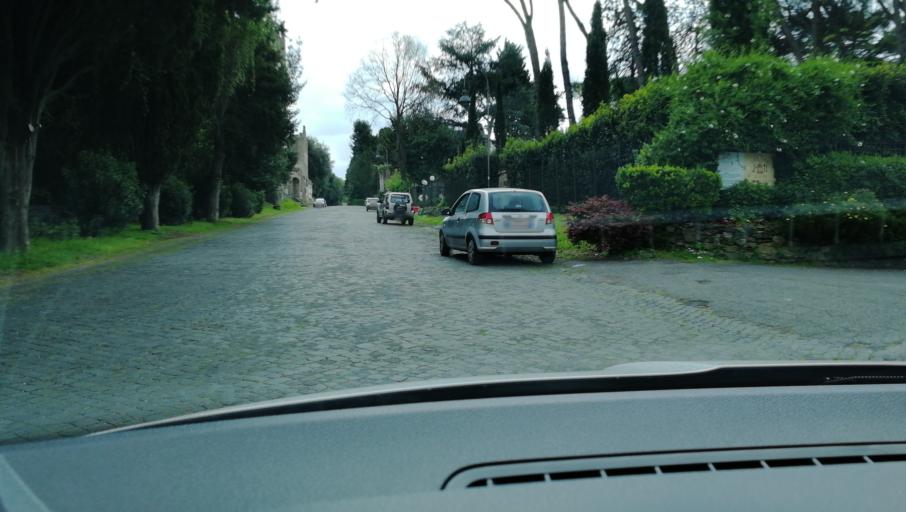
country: IT
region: Latium
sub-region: Citta metropolitana di Roma Capitale
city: Rome
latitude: 41.8528
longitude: 12.5197
